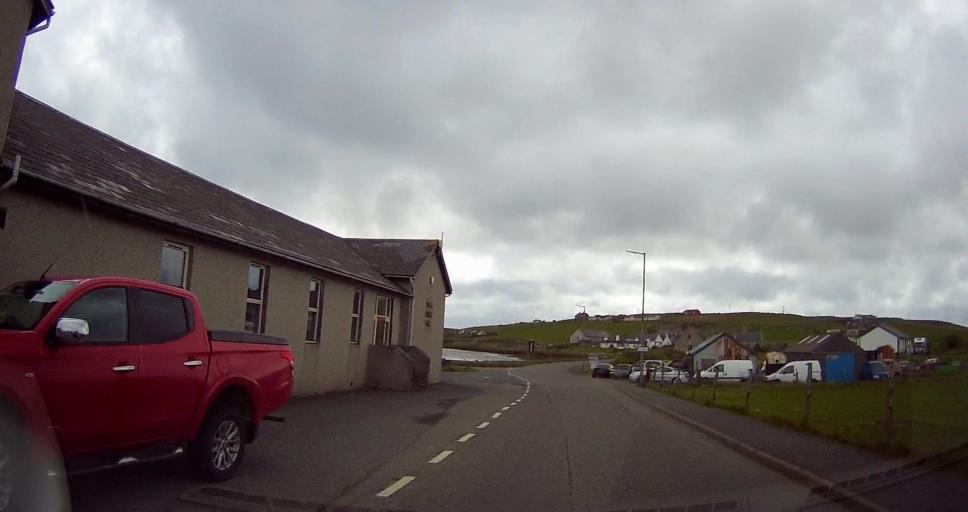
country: GB
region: Scotland
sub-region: Shetland Islands
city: Sandwick
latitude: 60.2297
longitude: -1.5627
